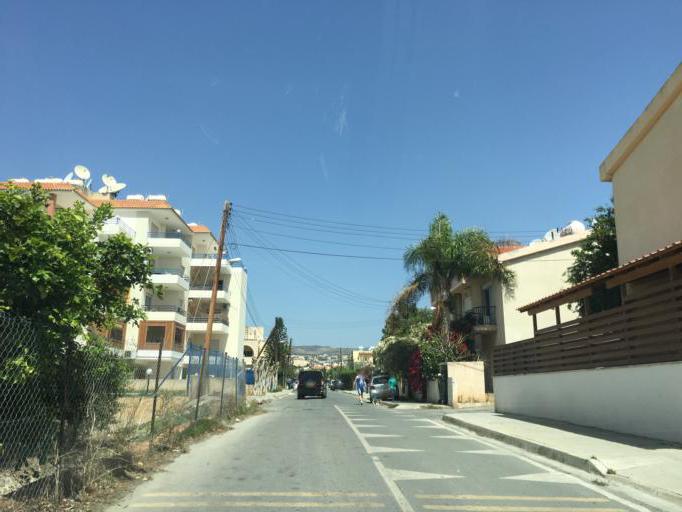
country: CY
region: Limassol
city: Mouttagiaka
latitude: 34.6981
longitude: 33.0868
